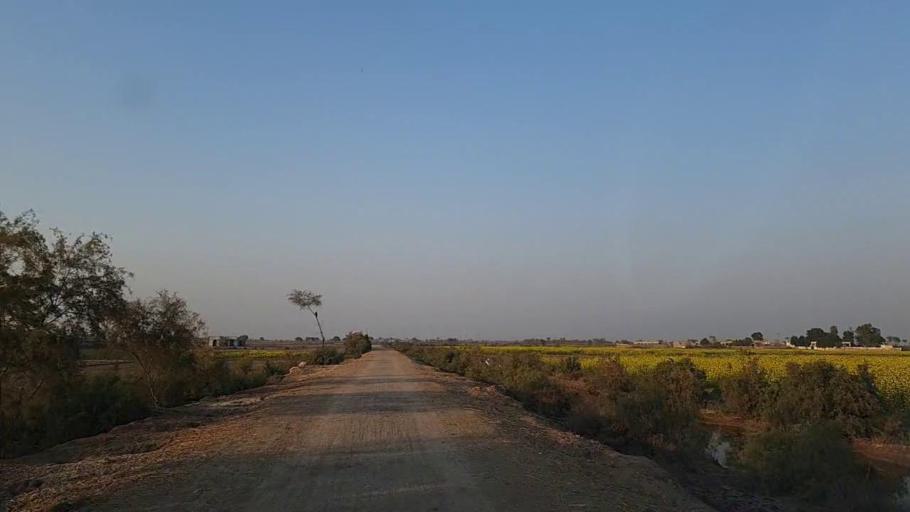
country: PK
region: Sindh
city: Bandhi
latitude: 26.5452
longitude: 68.3166
